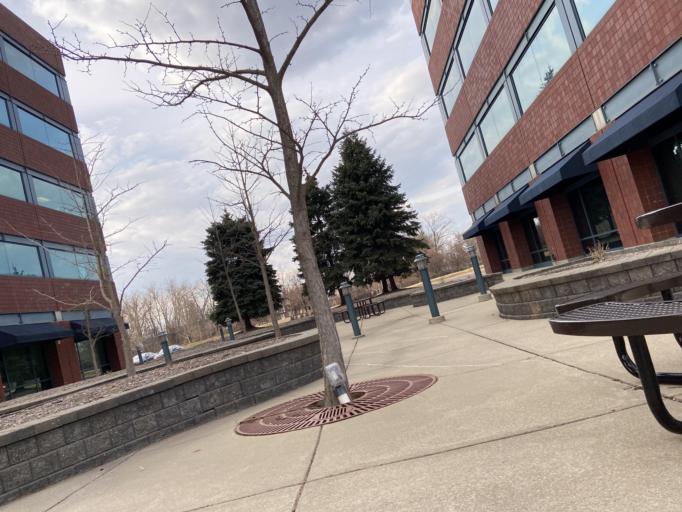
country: US
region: Michigan
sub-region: Oakland County
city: Southfield
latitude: 42.4818
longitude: -83.2493
